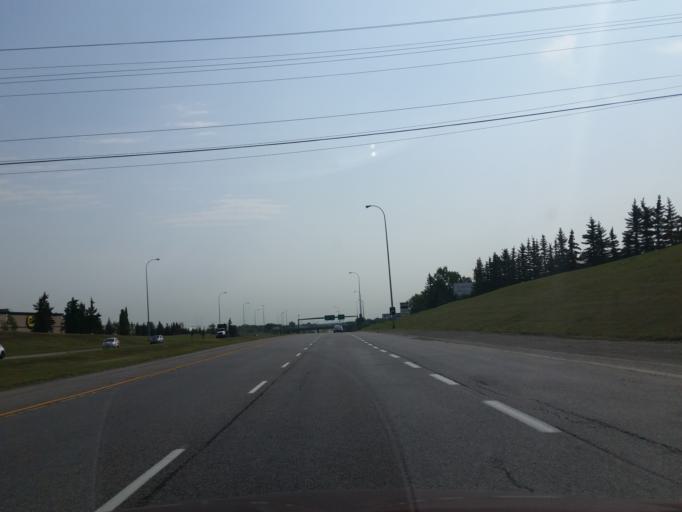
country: CA
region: Alberta
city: Calgary
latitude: 51.0668
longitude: -113.9939
